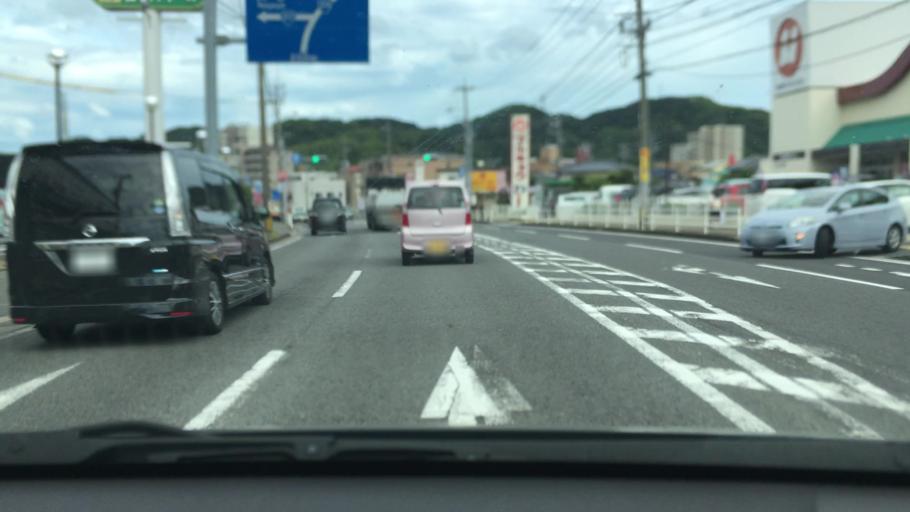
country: JP
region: Nagasaki
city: Togitsu
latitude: 32.8324
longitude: 129.8449
